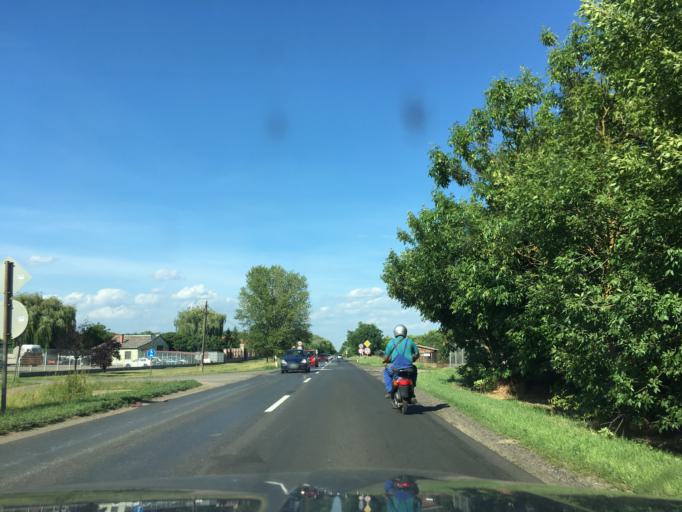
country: HU
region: Hajdu-Bihar
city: Hajdusamson
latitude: 47.5728
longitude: 21.6979
